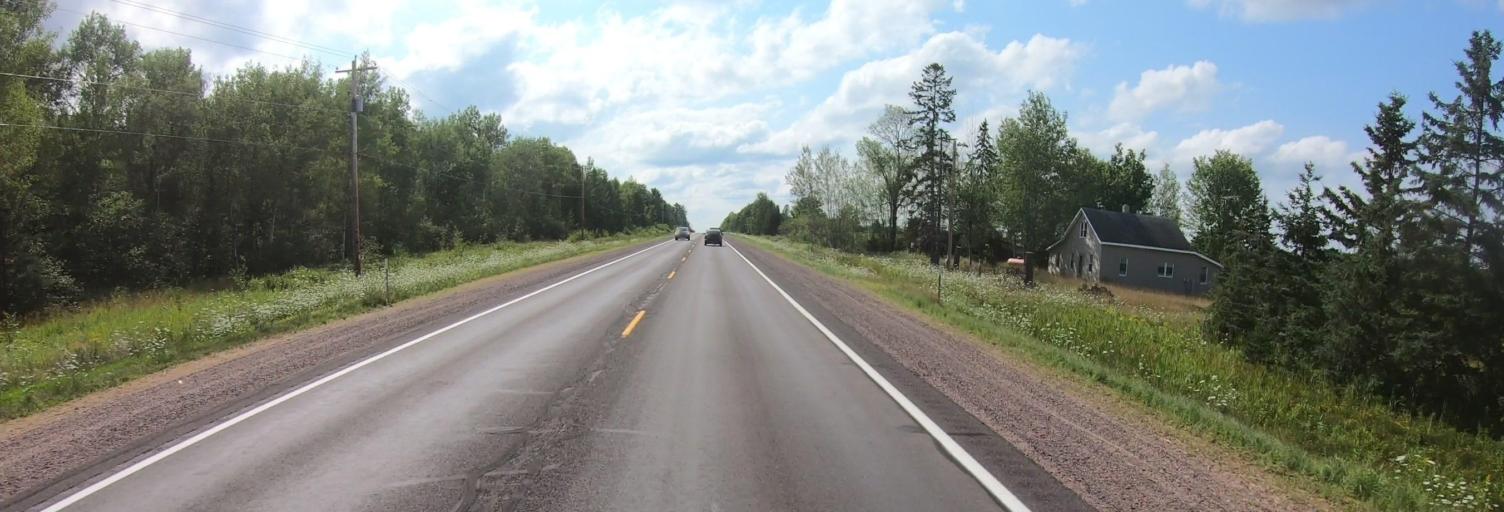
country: US
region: Michigan
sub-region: Ontonagon County
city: Ontonagon
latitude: 46.5348
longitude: -89.2446
